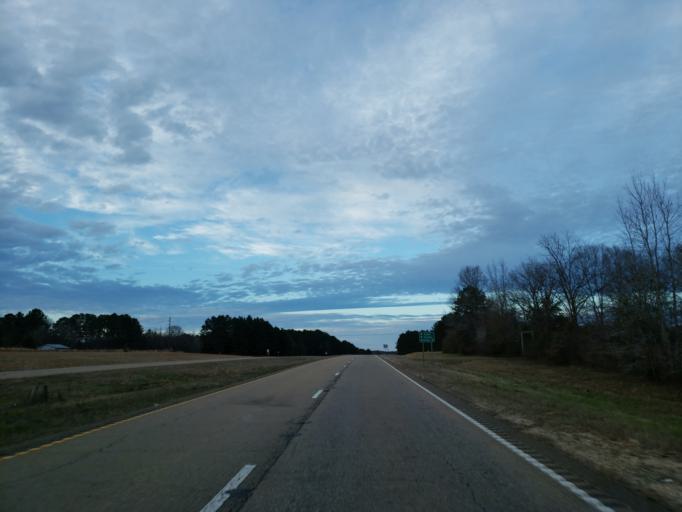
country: US
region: Mississippi
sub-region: Kemper County
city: De Kalb
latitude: 32.6836
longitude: -88.4893
